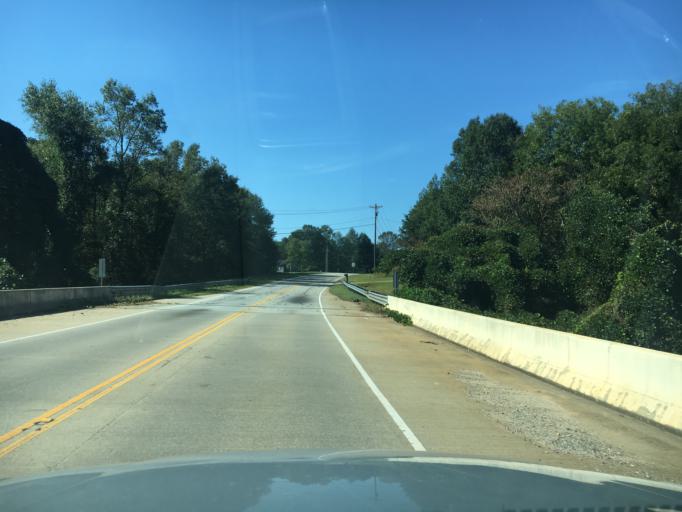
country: US
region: South Carolina
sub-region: Greenville County
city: Taylors
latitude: 34.9064
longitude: -82.2761
